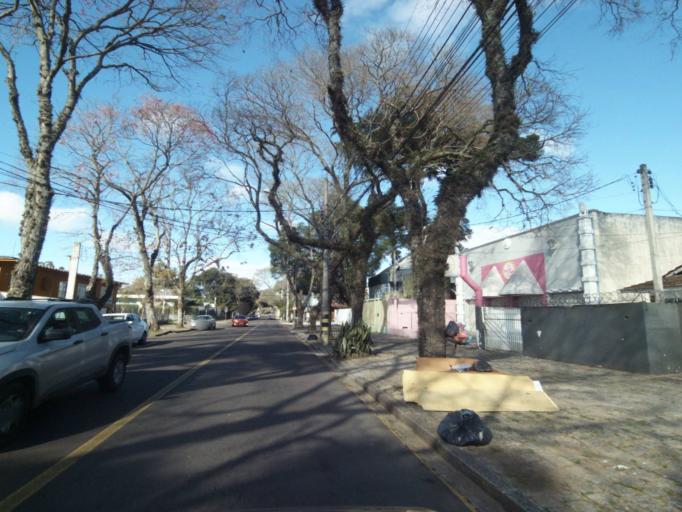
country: BR
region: Parana
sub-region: Curitiba
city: Curitiba
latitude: -25.4194
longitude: -49.2482
